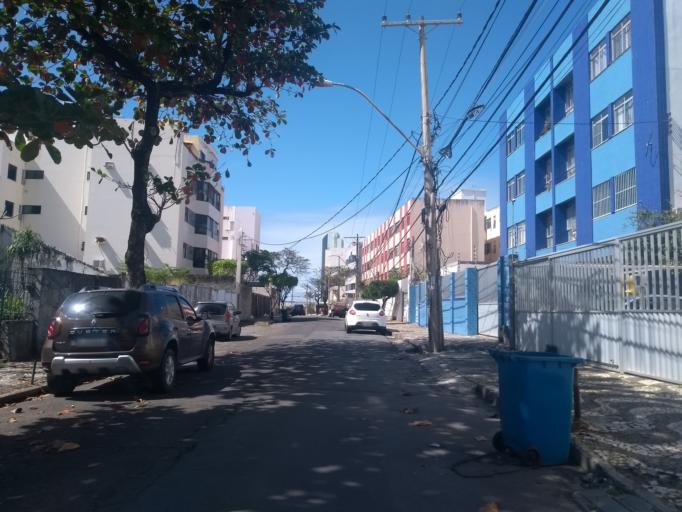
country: BR
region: Bahia
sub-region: Salvador
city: Salvador
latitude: -12.9963
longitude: -38.4482
